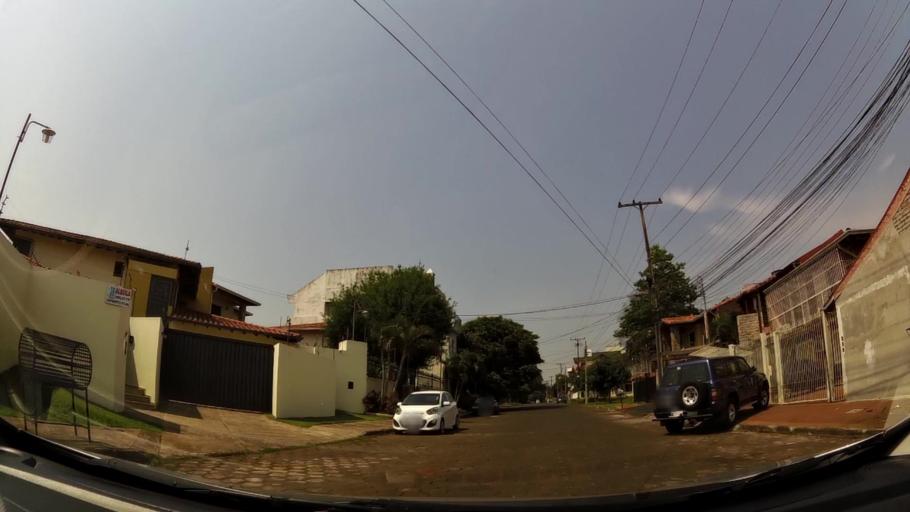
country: PY
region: Alto Parana
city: Presidente Franco
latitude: -25.5230
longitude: -54.6201
